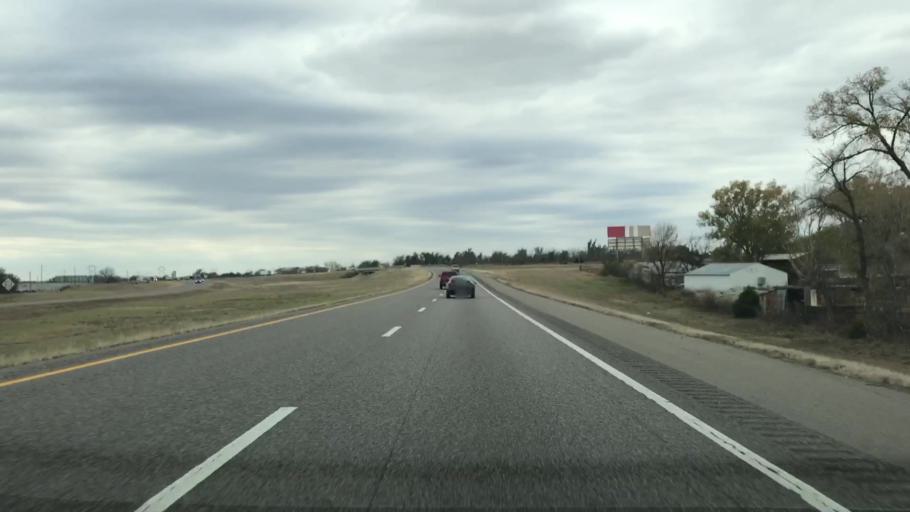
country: US
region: Oklahoma
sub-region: Beckham County
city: Elk City
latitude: 35.3858
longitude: -99.5073
